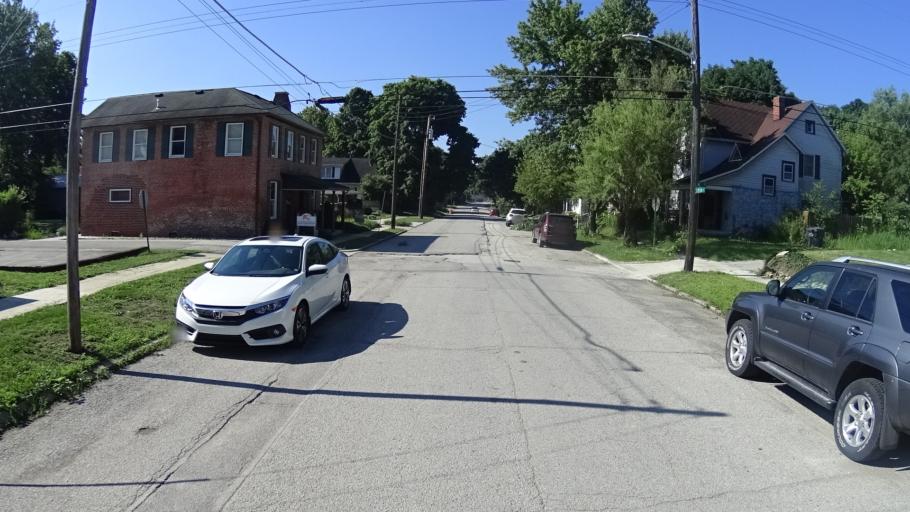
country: US
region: Indiana
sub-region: Madison County
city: Pendleton
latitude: 40.0002
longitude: -85.7473
